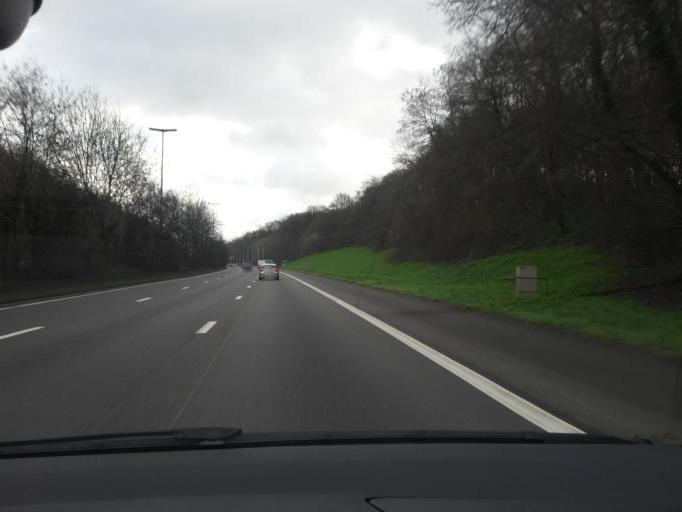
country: BE
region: Wallonia
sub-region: Province du Brabant Wallon
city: Wavre
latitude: 50.7268
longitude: 4.5642
